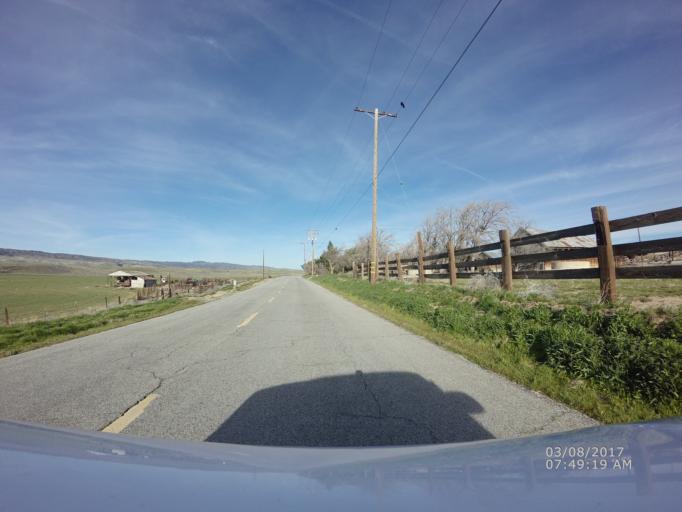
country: US
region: California
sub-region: Los Angeles County
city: Green Valley
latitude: 34.7136
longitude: -118.3559
